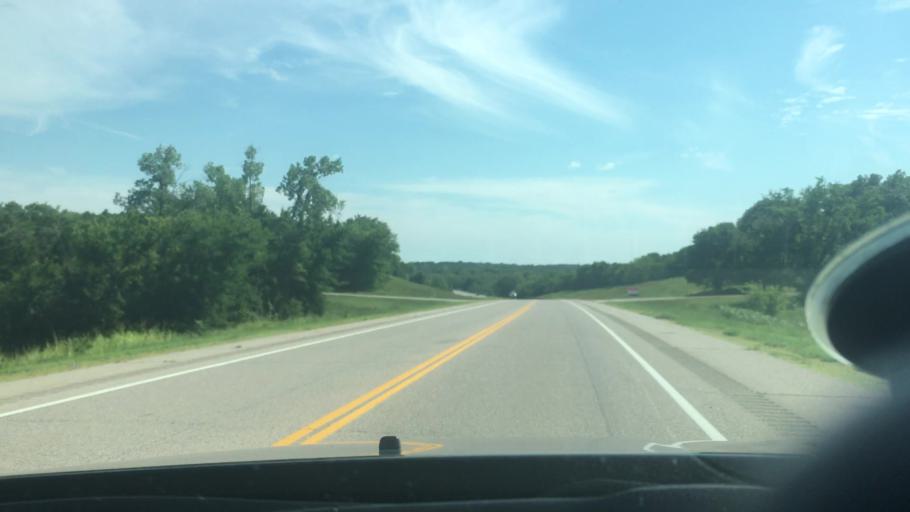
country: US
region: Oklahoma
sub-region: Seminole County
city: Seminole
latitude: 35.1361
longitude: -96.6777
